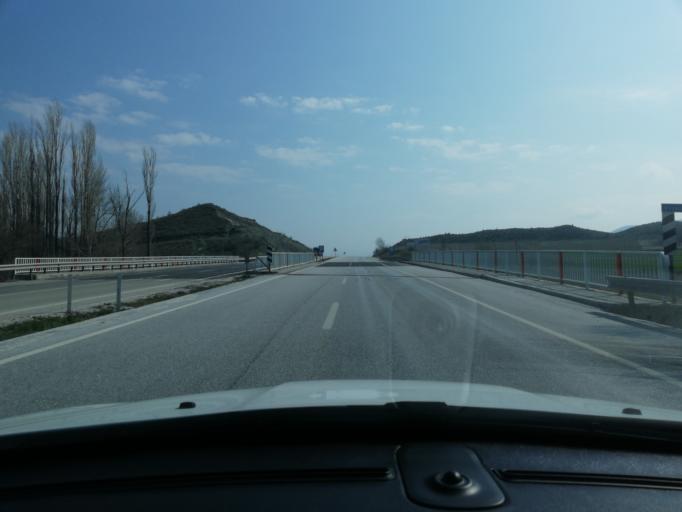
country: TR
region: Cankiri
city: Beloren
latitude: 40.8772
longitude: 33.5104
